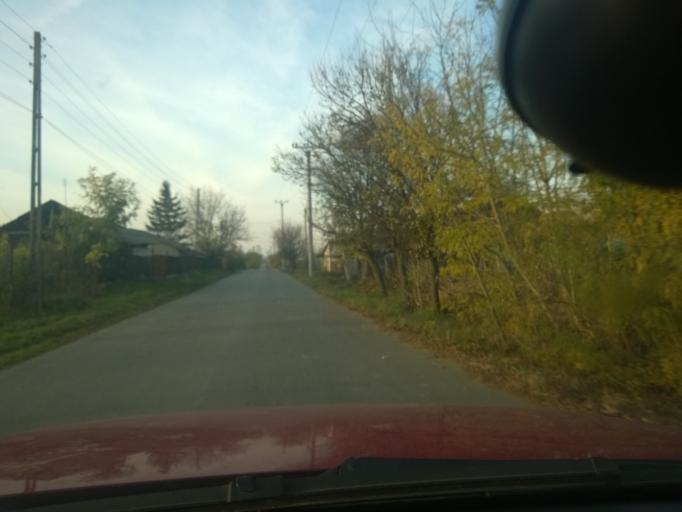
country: RO
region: Giurgiu
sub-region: Comuna Herasti
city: Herasti
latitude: 44.2146
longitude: 26.3592
